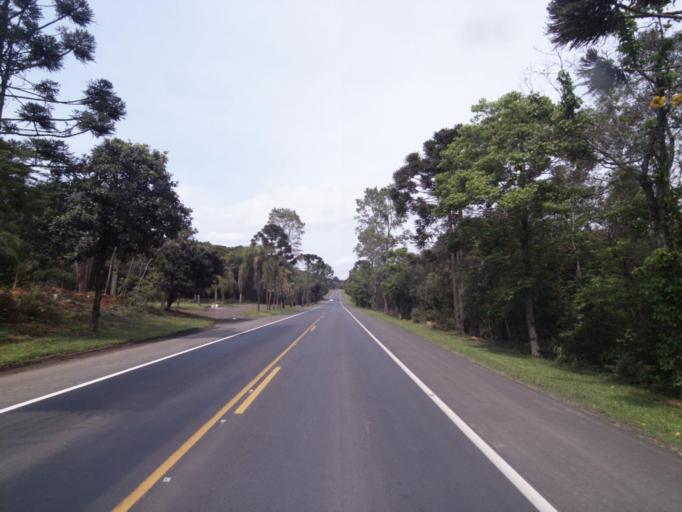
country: BR
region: Parana
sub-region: Irati
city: Irati
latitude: -25.4669
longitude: -50.5193
